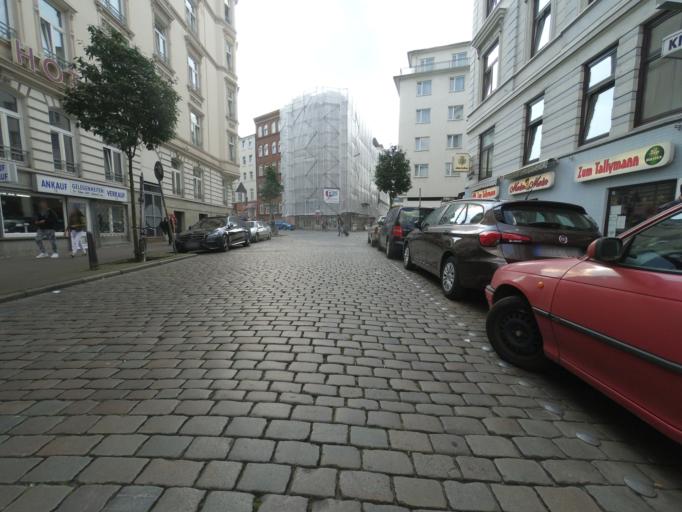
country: DE
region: Hamburg
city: St. Georg
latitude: 53.5538
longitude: 10.0102
